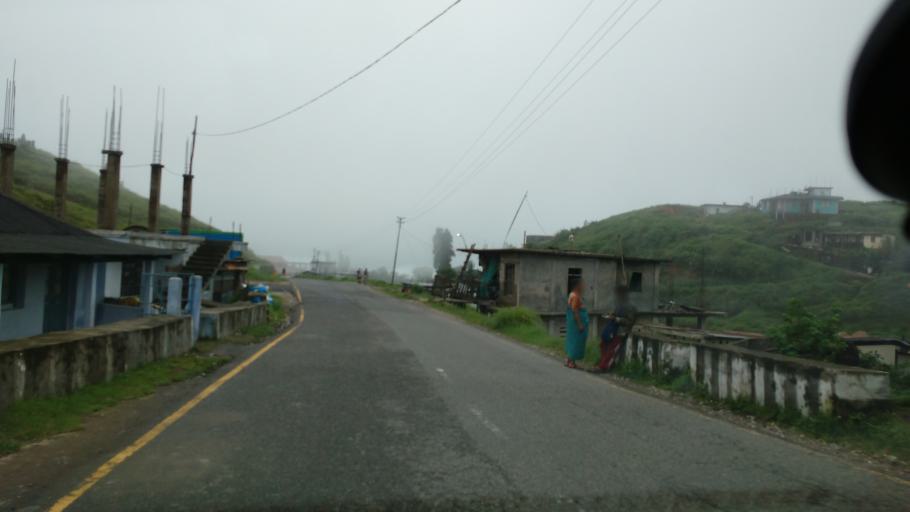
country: IN
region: Meghalaya
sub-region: East Khasi Hills
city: Cherrapunji
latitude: 25.2785
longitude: 91.7286
